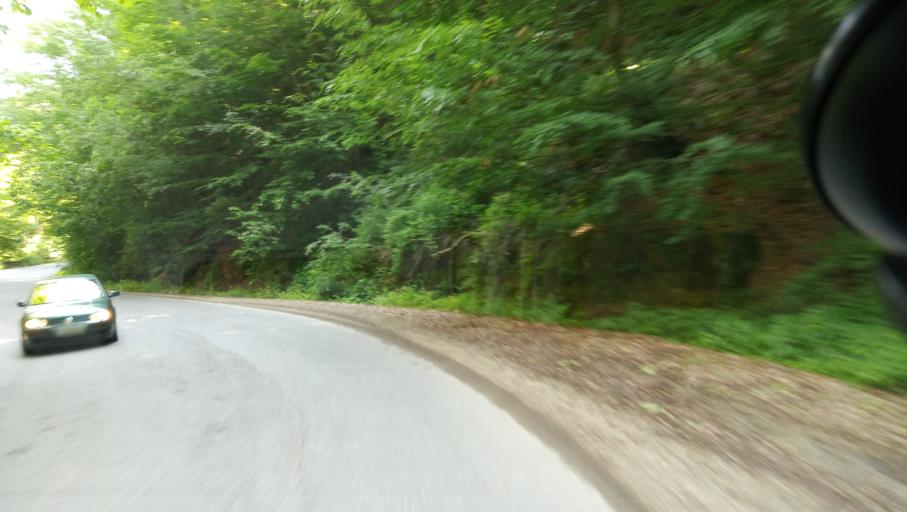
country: RO
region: Cluj
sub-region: Comuna Capusu Mare
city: Capusu Mare
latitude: 46.7125
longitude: 23.2728
